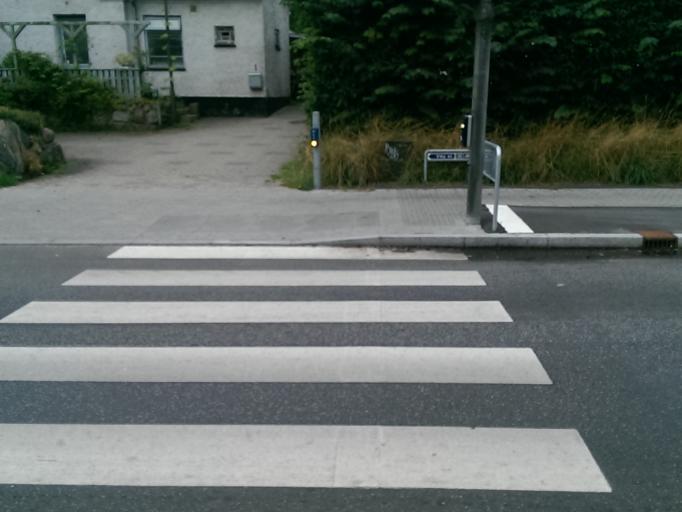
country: DK
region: Zealand
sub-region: Roskilde Kommune
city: Viby
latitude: 55.5512
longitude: 12.0257
